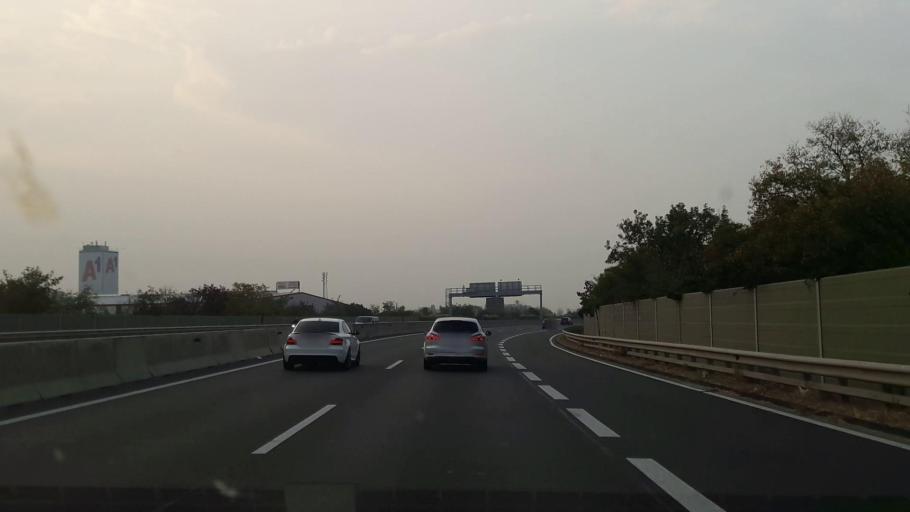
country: AT
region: Lower Austria
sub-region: Politischer Bezirk Wien-Umgebung
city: Schwechat
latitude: 48.1518
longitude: 16.4833
